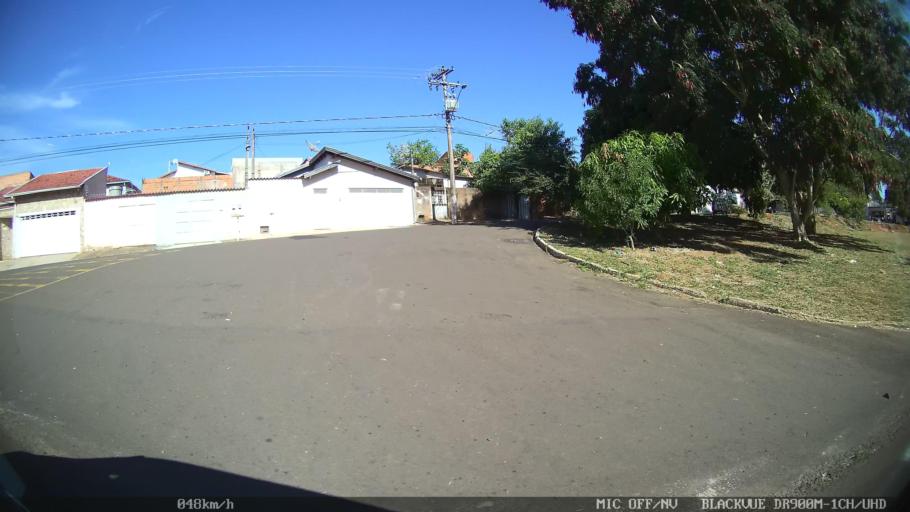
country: BR
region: Sao Paulo
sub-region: Franca
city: Franca
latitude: -20.4925
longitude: -47.4268
